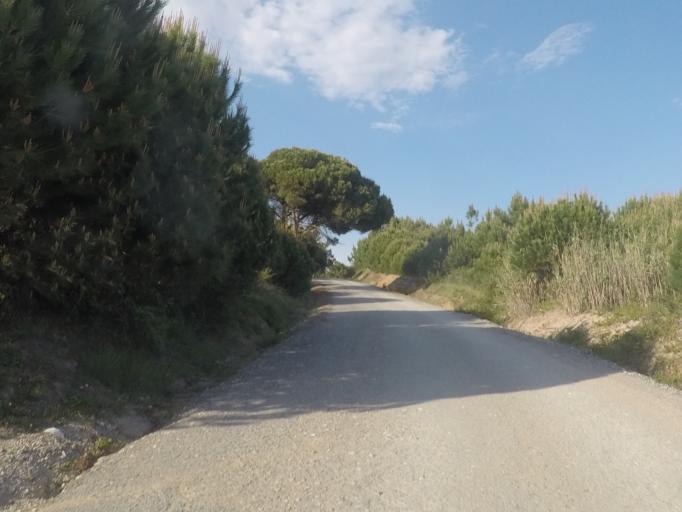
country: PT
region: Setubal
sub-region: Sesimbra
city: Sesimbra
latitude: 38.4580
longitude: -9.1872
